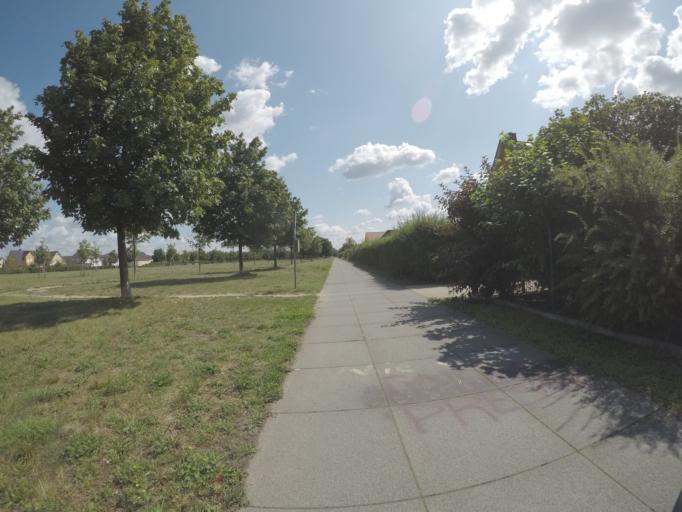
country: DE
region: Berlin
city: Biesdorf
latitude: 52.5024
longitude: 13.5666
